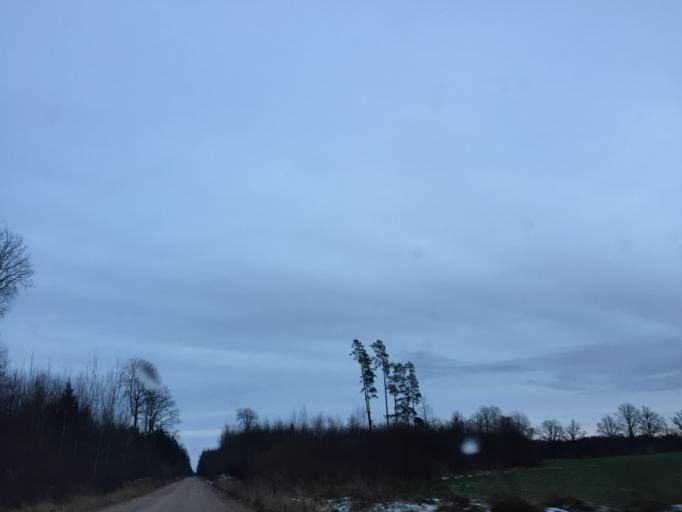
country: LV
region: Burtnieki
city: Matisi
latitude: 57.6326
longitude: 25.1201
